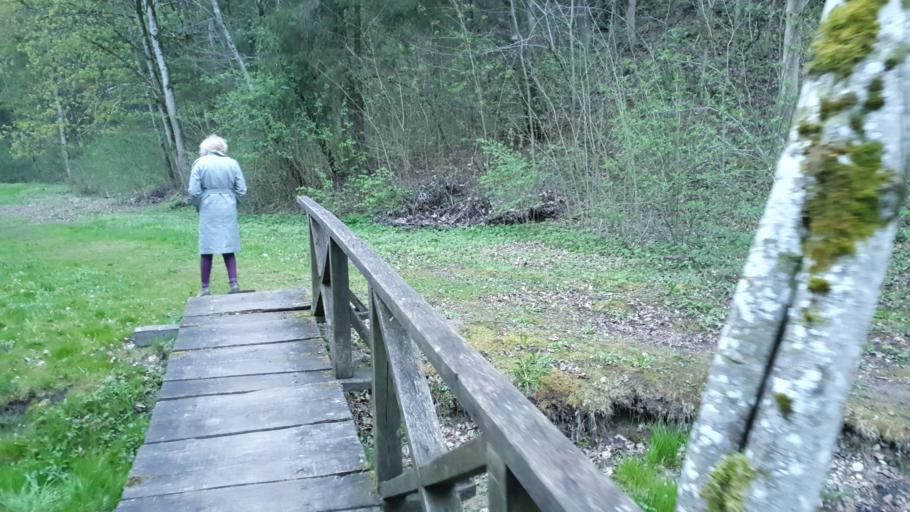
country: LT
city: Sakiai
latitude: 55.0792
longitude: 23.1788
